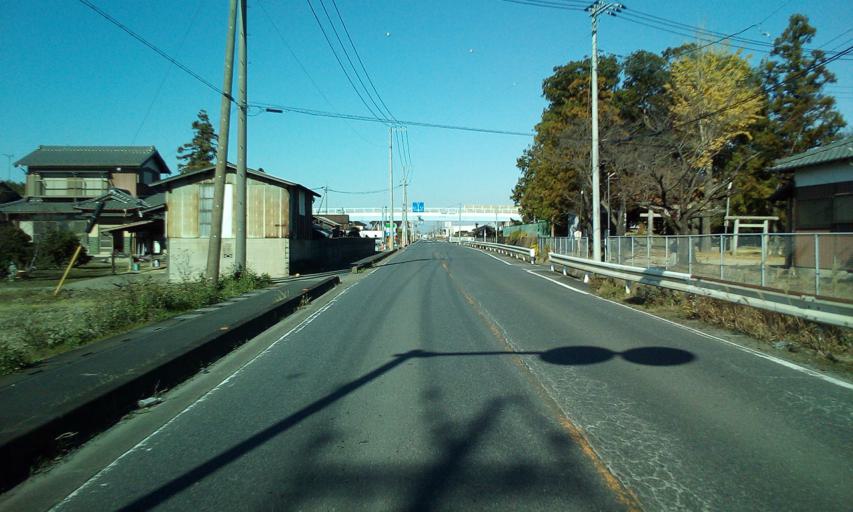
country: JP
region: Saitama
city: Sugito
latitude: 36.0355
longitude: 139.7860
